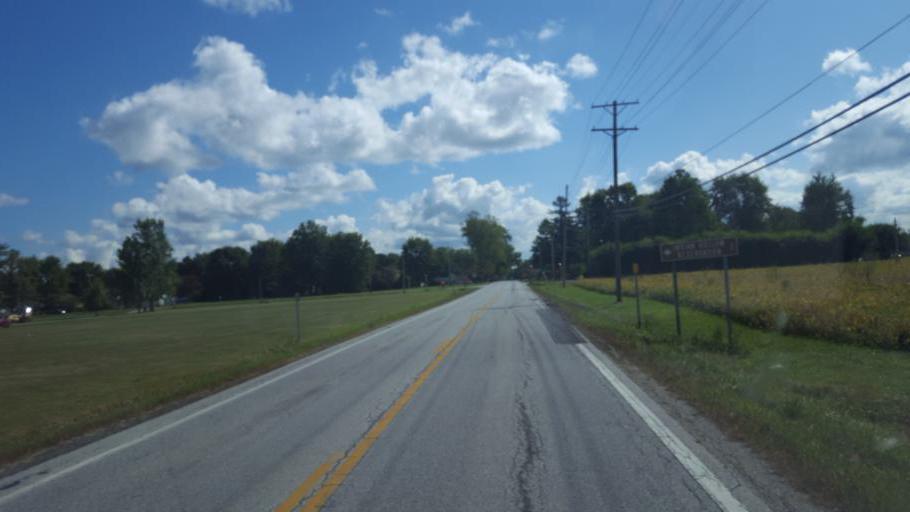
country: US
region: Ohio
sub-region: Lorain County
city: Lagrange
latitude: 41.2373
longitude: -82.0877
